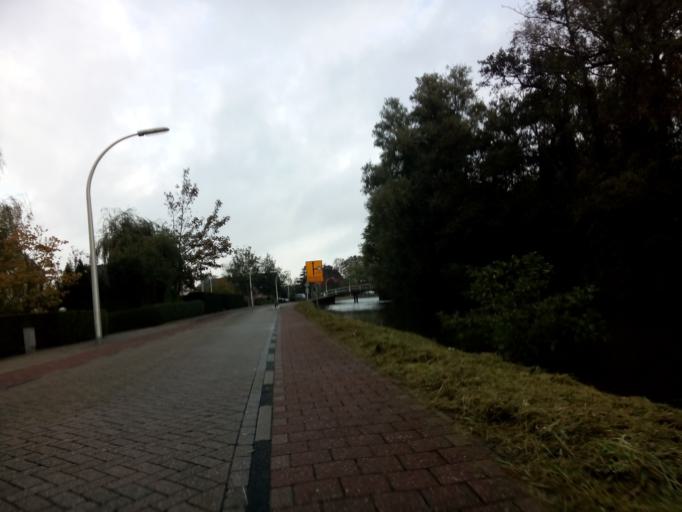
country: NL
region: South Holland
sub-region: Gemeente Maassluis
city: Maassluis
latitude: 51.9312
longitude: 4.2695
